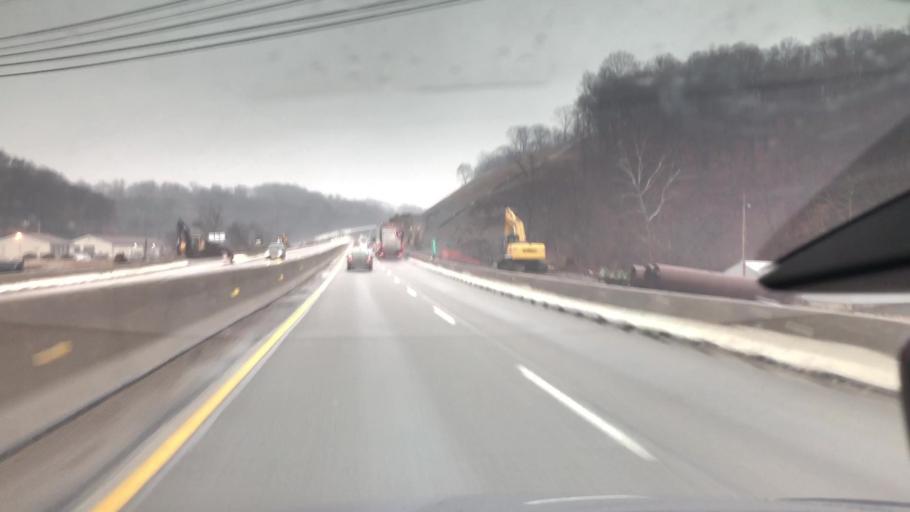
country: US
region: Pennsylvania
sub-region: Allegheny County
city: Russellton
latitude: 40.5874
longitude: -79.8796
